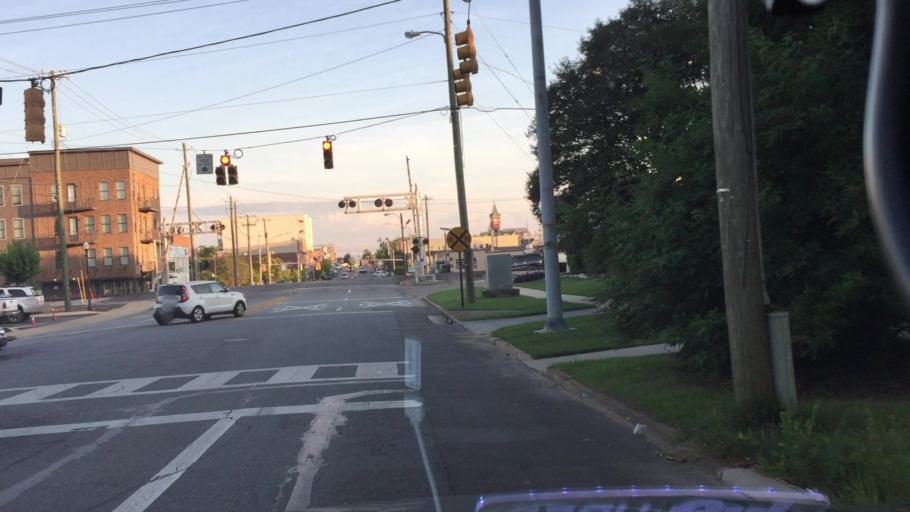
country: US
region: Alabama
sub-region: Lee County
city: Auburn
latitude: 32.6106
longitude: -85.4818
